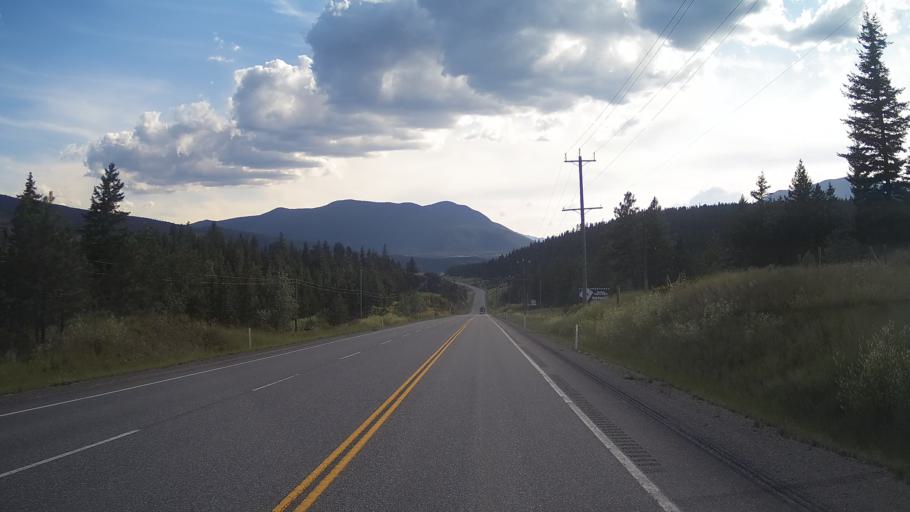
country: CA
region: British Columbia
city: Cache Creek
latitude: 51.1242
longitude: -121.5249
